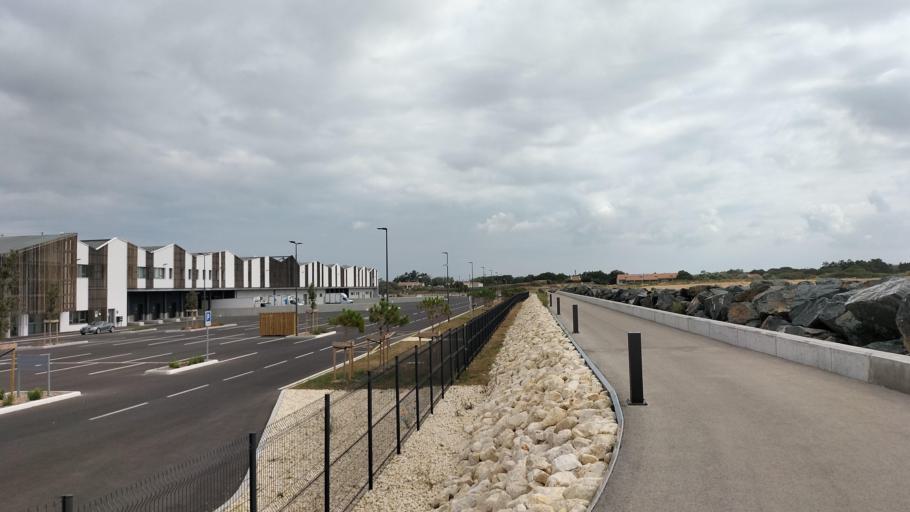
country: FR
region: Poitou-Charentes
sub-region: Departement de la Charente-Maritime
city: Dolus-d'Oleron
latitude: 45.9104
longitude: -1.3255
